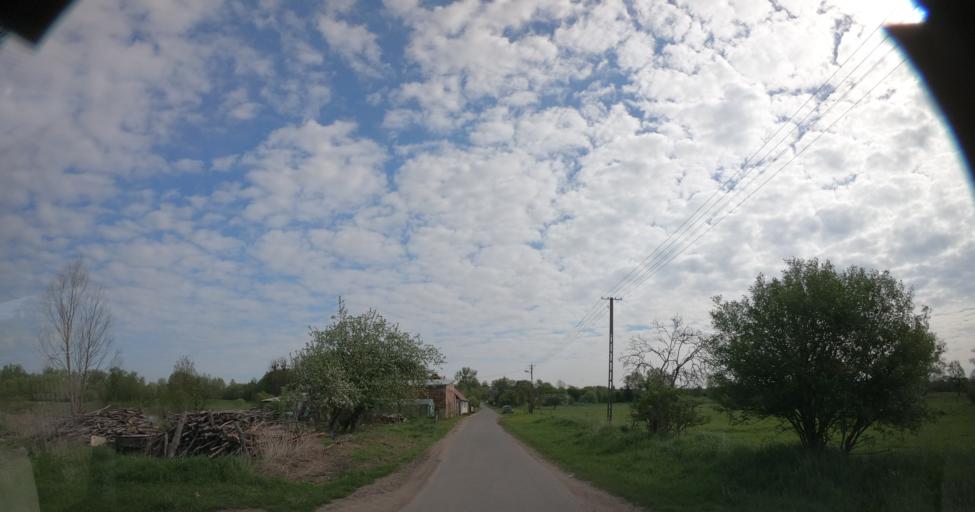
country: PL
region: West Pomeranian Voivodeship
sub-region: Powiat stargardzki
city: Suchan
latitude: 53.2689
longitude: 15.3542
